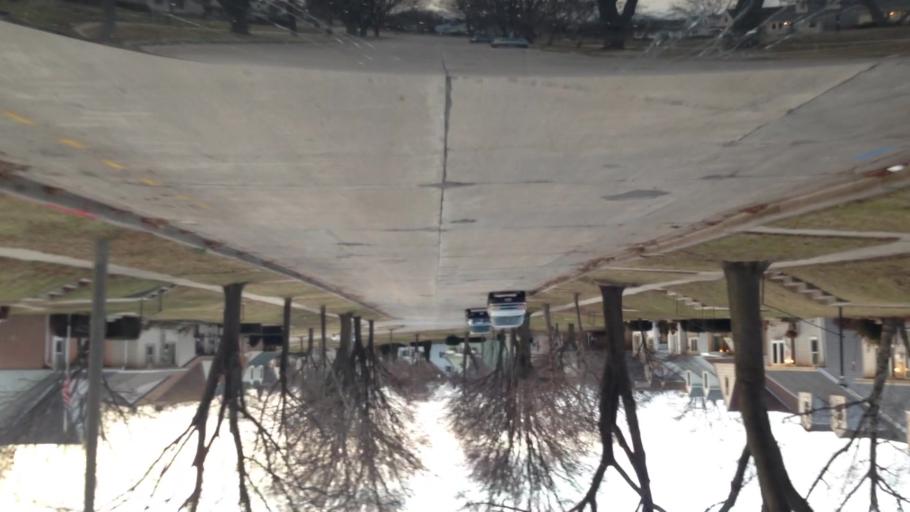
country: US
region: Wisconsin
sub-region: Milwaukee County
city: West Milwaukee
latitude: 42.9986
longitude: -87.9901
